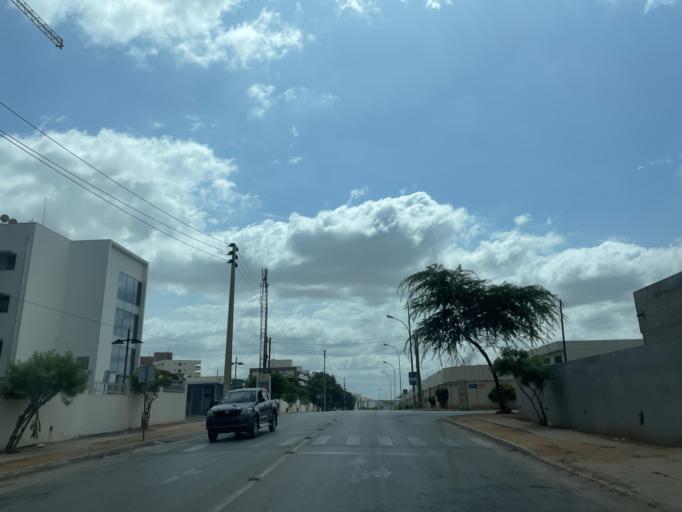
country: AO
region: Luanda
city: Luanda
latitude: -8.9262
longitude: 13.1842
